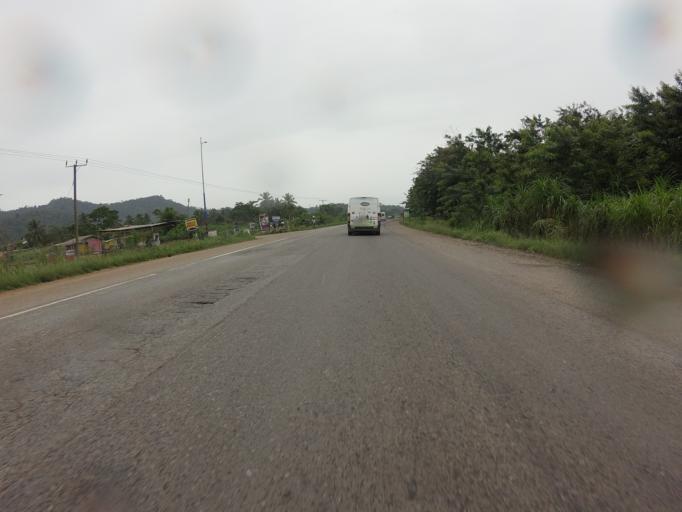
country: GH
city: Kibi
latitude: 6.1266
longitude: -0.4953
